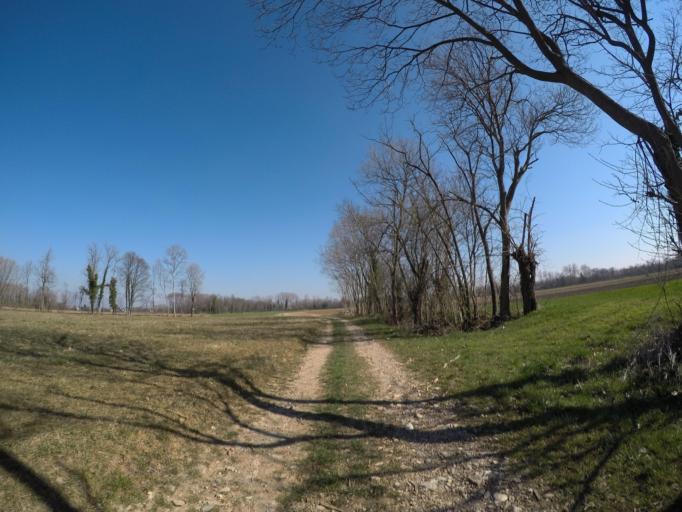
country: IT
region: Friuli Venezia Giulia
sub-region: Provincia di Udine
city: Pozzuolo del Friuli
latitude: 45.9847
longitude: 13.1799
